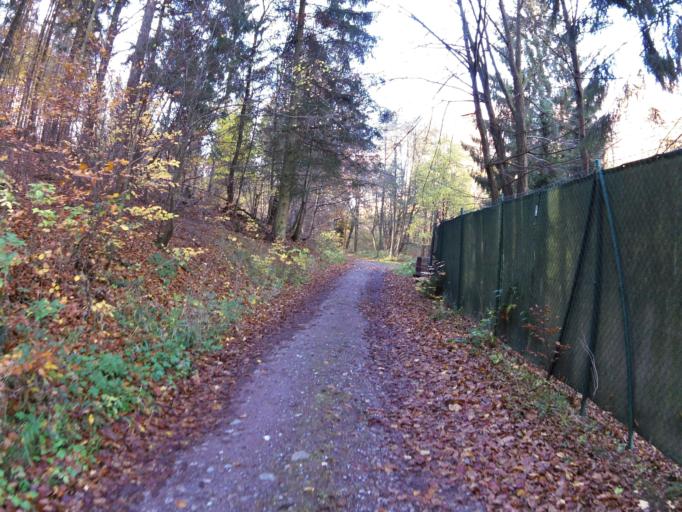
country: DE
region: Thuringia
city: Ruhla
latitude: 50.9008
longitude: 10.3517
